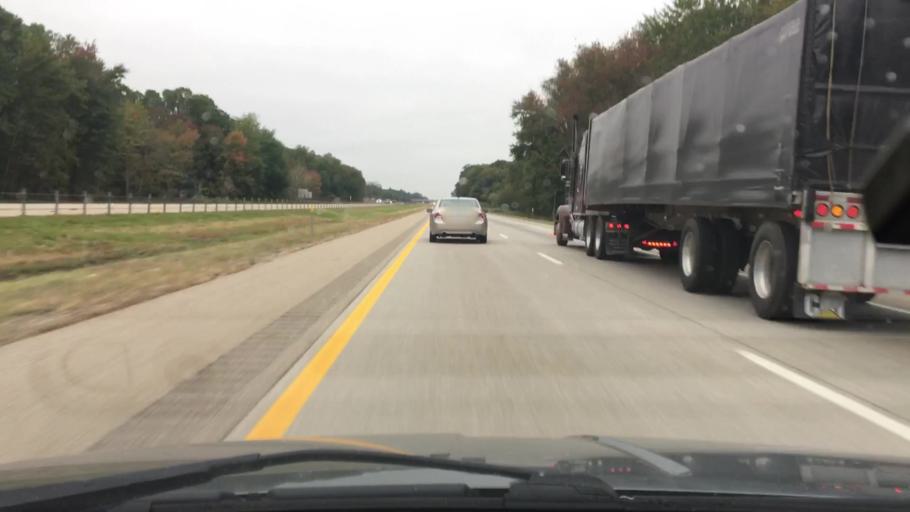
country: US
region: Michigan
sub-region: Van Buren County
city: Mattawan
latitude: 42.2212
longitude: -85.8092
